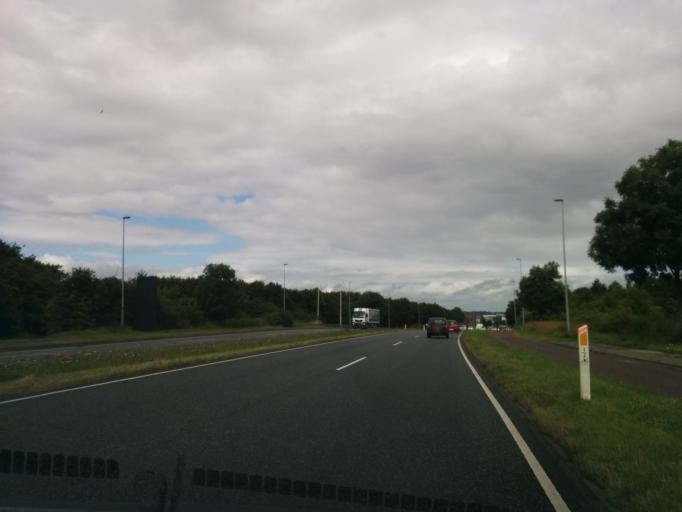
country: DK
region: Central Jutland
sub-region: Arhus Kommune
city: Arhus
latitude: 56.1903
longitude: 10.1901
